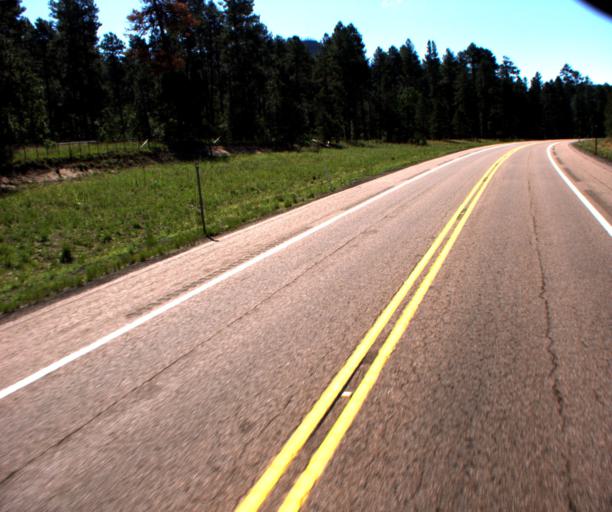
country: US
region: Arizona
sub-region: Apache County
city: Eagar
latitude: 33.8983
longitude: -109.1564
